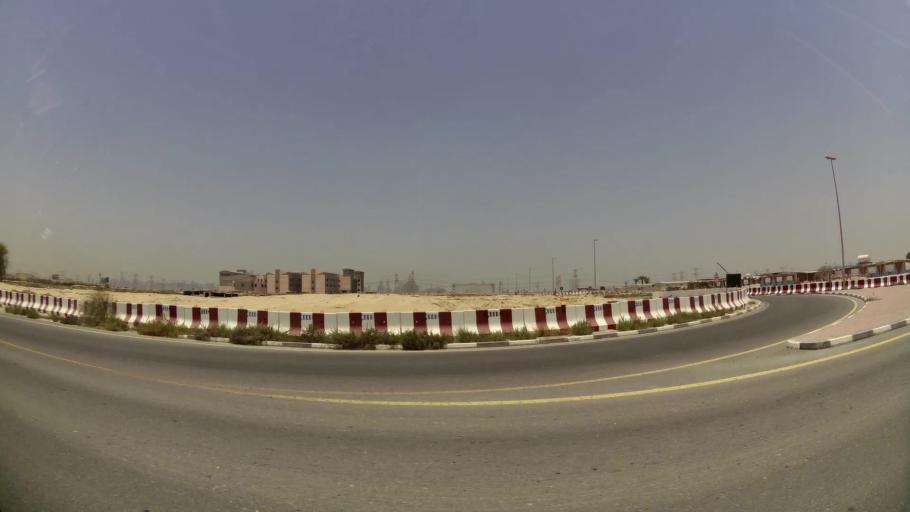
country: AE
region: Dubai
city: Dubai
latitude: 25.0736
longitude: 55.2191
